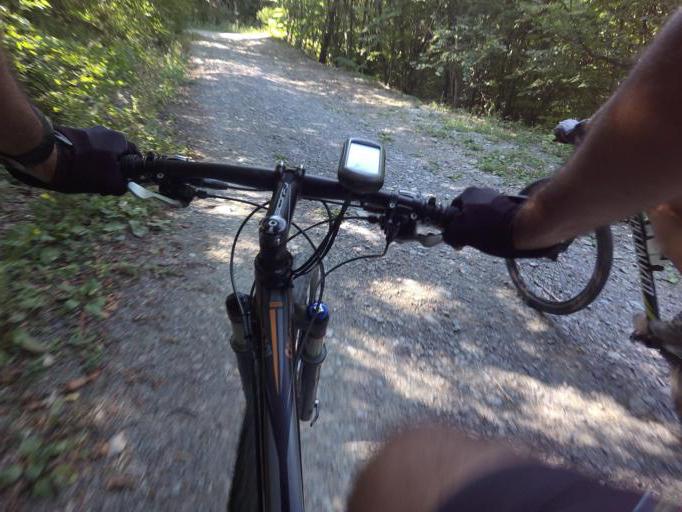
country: IT
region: Emilia-Romagna
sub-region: Provincia di Modena
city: Montecreto
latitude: 44.2391
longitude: 10.7264
